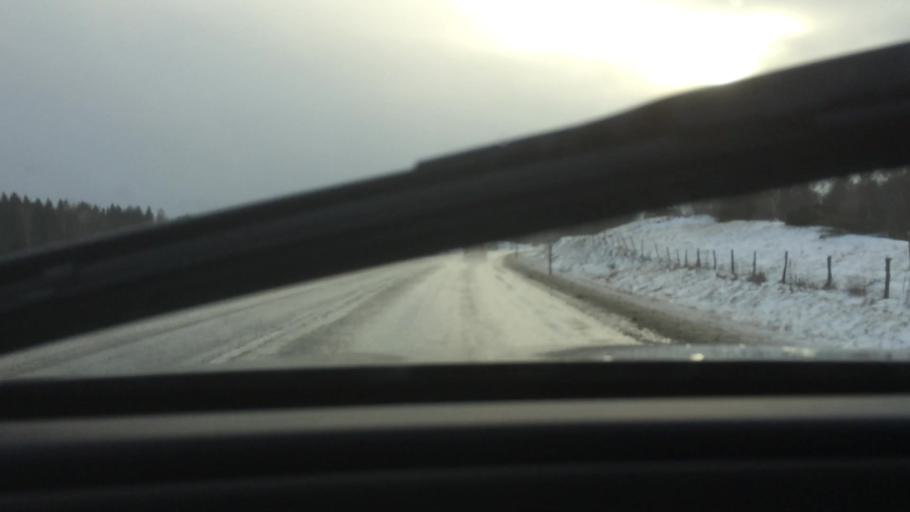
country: SE
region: Vaestra Goetaland
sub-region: Falkopings Kommun
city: Falkoeping
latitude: 57.9746
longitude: 13.5291
